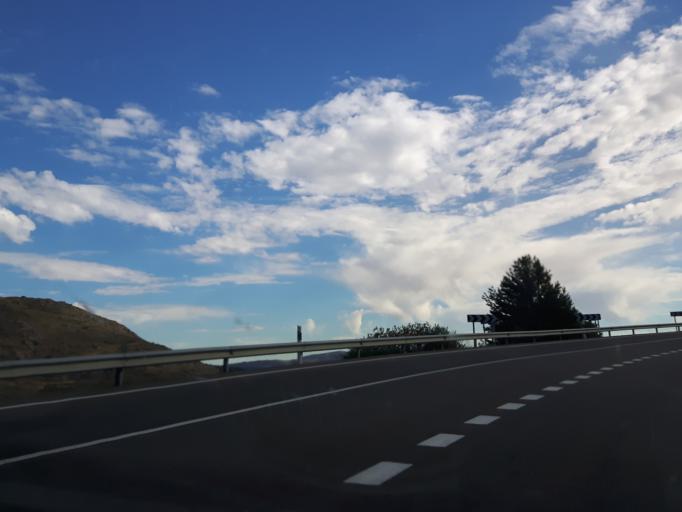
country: ES
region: Castille and Leon
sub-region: Provincia de Avila
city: Mengamunoz
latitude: 40.4866
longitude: -5.0078
